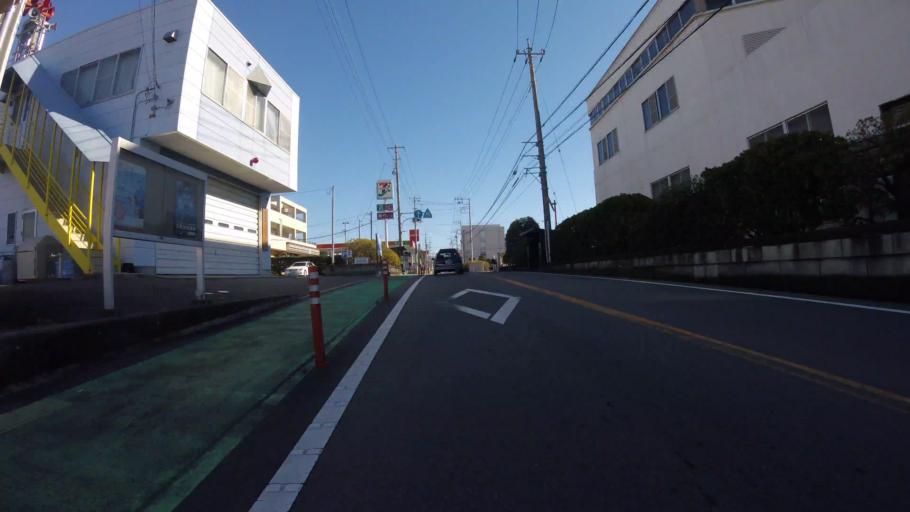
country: JP
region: Shizuoka
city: Mishima
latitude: 35.1201
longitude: 138.8917
